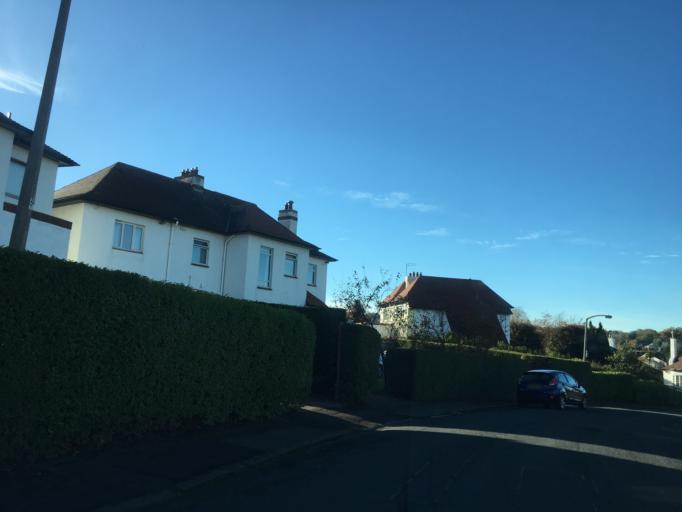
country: GB
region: Scotland
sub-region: Edinburgh
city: Edinburgh
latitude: 55.9518
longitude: -3.2421
